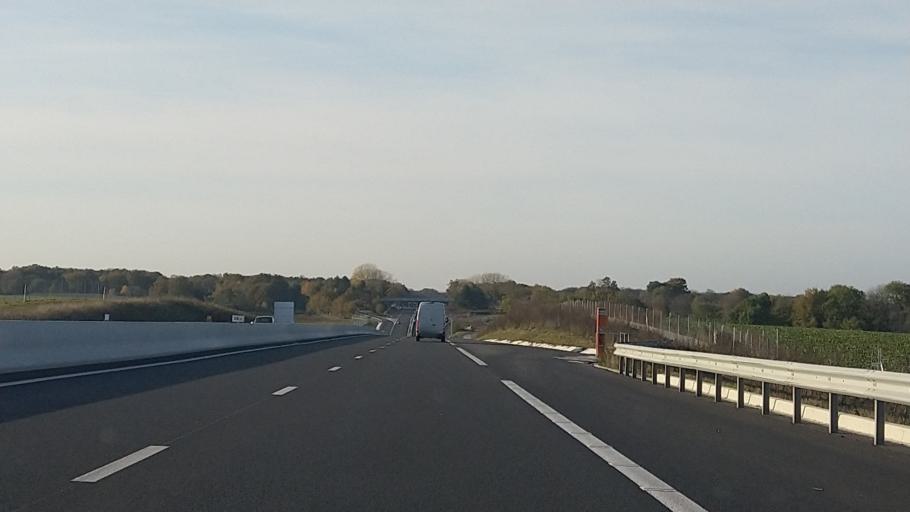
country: FR
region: Ile-de-France
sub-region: Departement du Val-d'Oise
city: Maffliers
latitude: 49.0985
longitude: 2.2899
